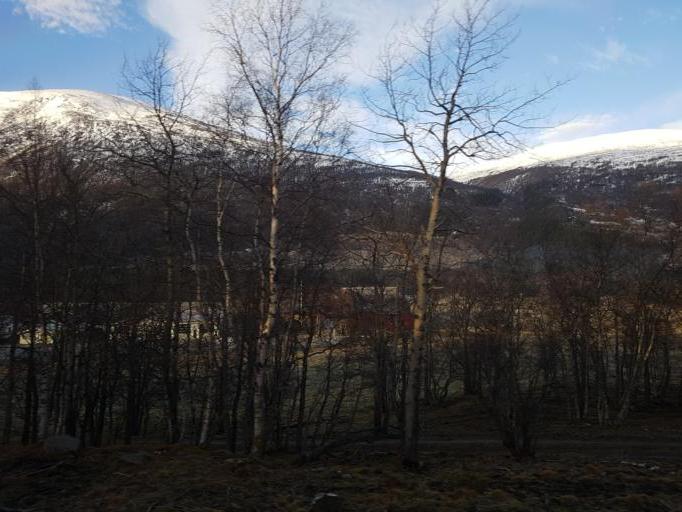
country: NO
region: Sor-Trondelag
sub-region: Oppdal
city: Oppdal
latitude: 62.5318
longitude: 9.6185
